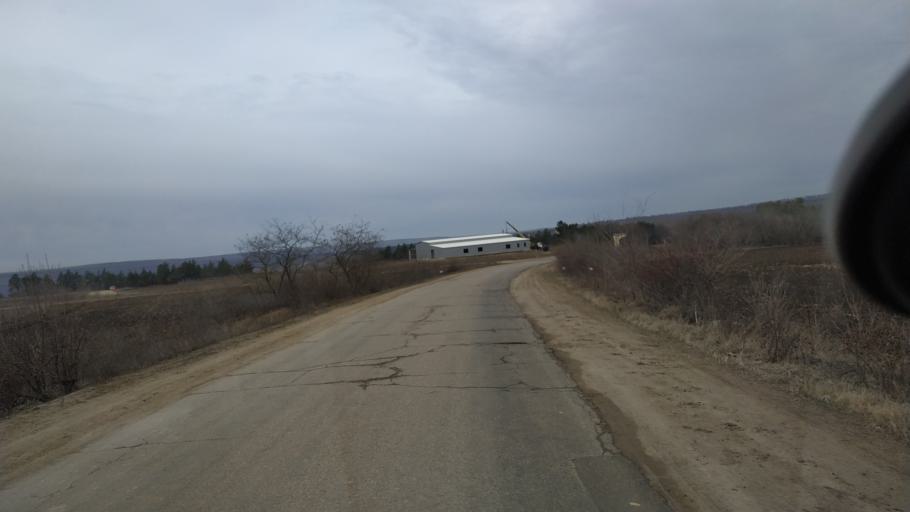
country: MD
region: Telenesti
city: Cocieri
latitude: 47.2665
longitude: 29.0834
